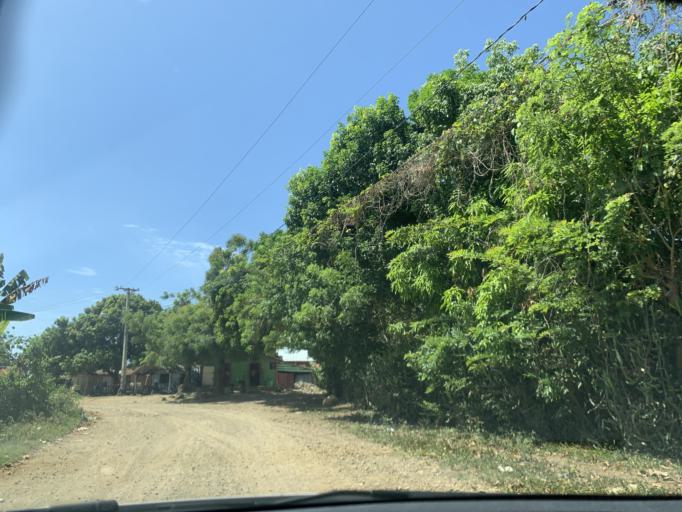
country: DO
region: Puerto Plata
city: Luperon
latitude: 19.8892
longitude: -70.8763
